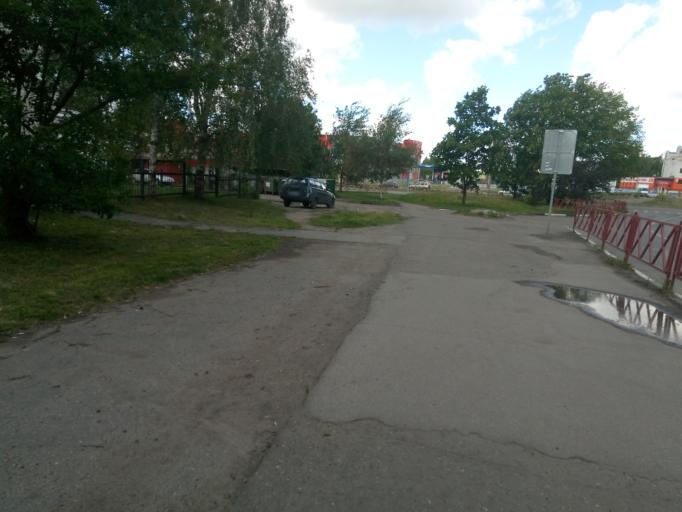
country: RU
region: Jaroslavl
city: Yaroslavl
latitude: 57.6581
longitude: 39.9554
